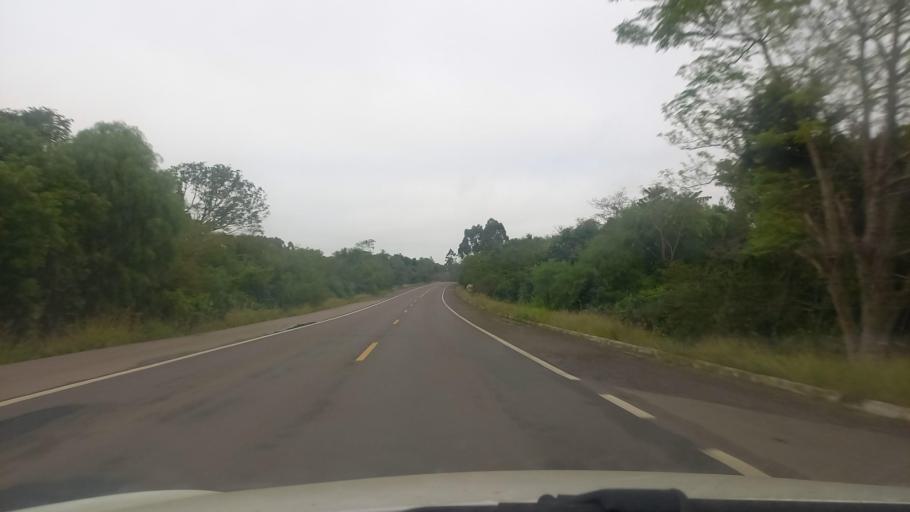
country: BR
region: Rio Grande do Sul
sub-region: Sao Pedro Do Sul
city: Sao Pedro do Sul
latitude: -29.7818
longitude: -54.1059
